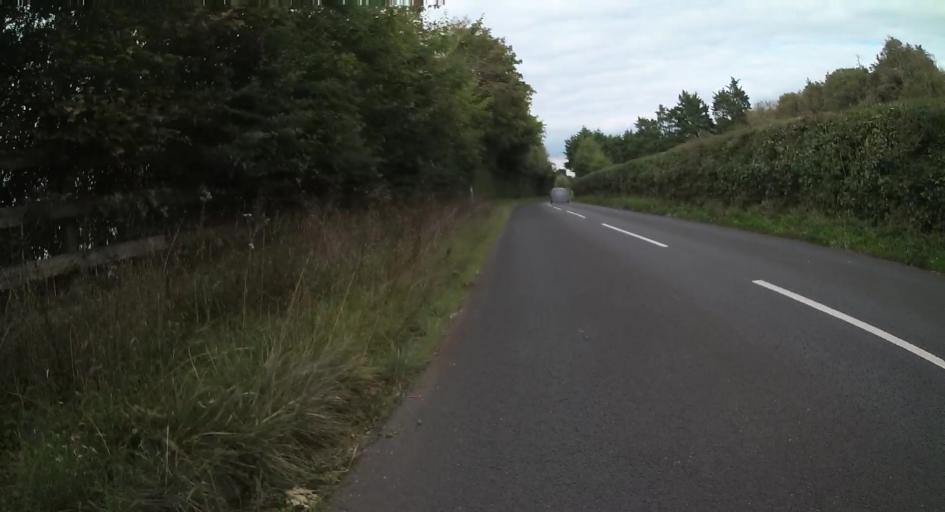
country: GB
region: England
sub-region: Isle of Wight
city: Freshwater
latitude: 50.6864
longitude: -1.4925
